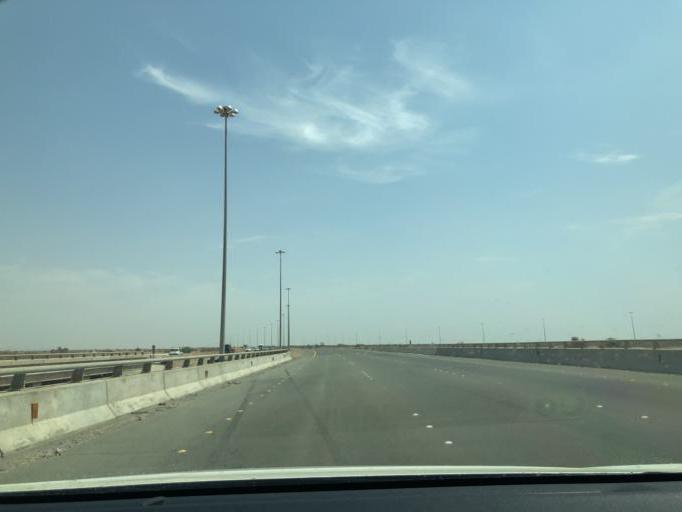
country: SA
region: Makkah
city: Rabigh
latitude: 22.2444
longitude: 39.1139
